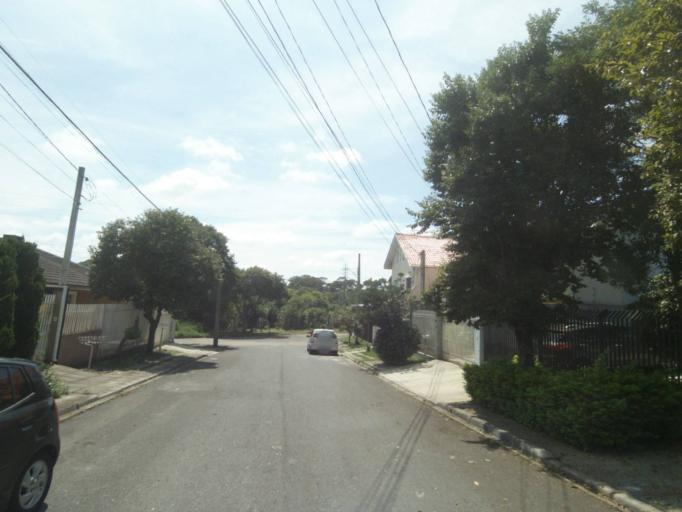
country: BR
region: Parana
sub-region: Curitiba
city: Curitiba
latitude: -25.4585
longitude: -49.3559
